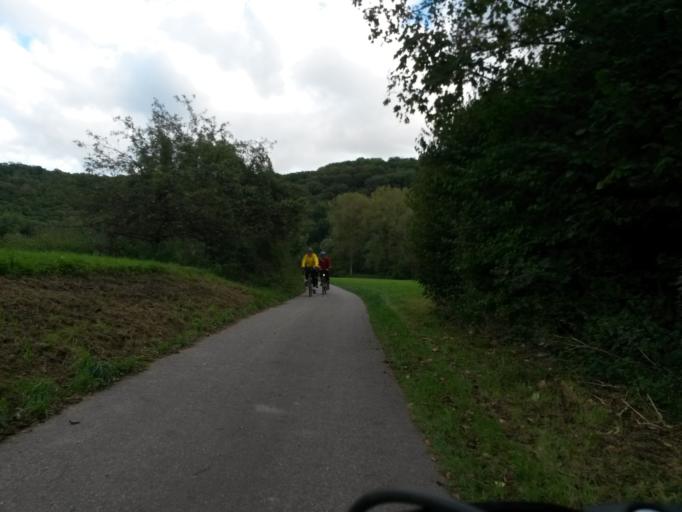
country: DE
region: Baden-Wuerttemberg
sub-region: Regierungsbezirk Stuttgart
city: Markgroningen
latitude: 48.9290
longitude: 9.0764
